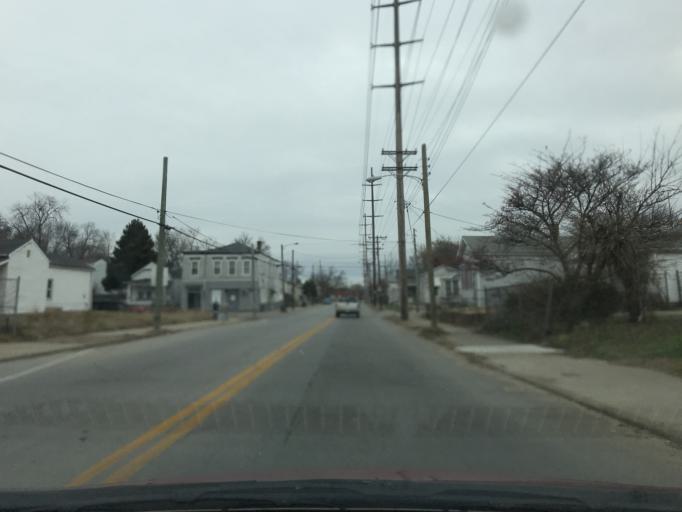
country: US
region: Kentucky
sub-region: Jefferson County
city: Louisville
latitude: 38.2638
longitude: -85.7854
